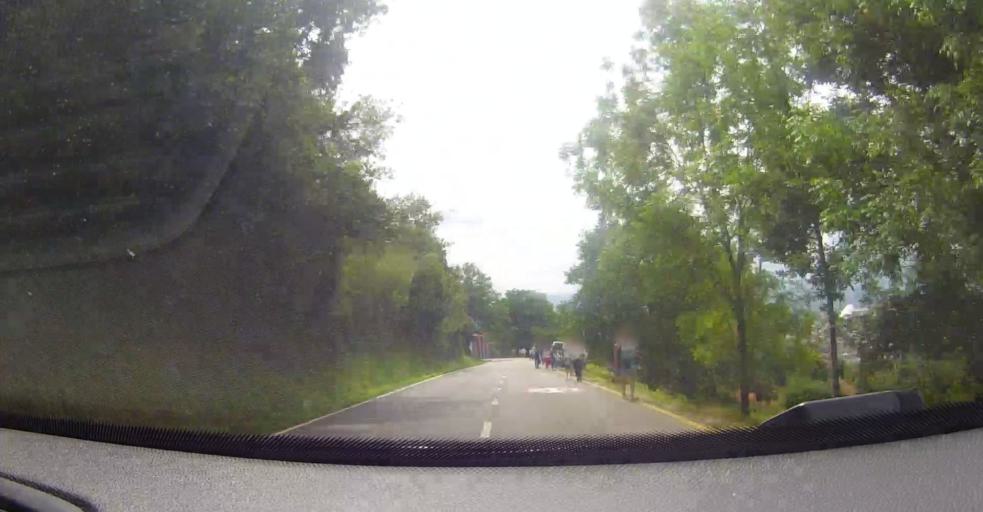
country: ES
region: Asturias
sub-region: Province of Asturias
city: Oviedo
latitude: 43.3799
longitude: -5.8672
